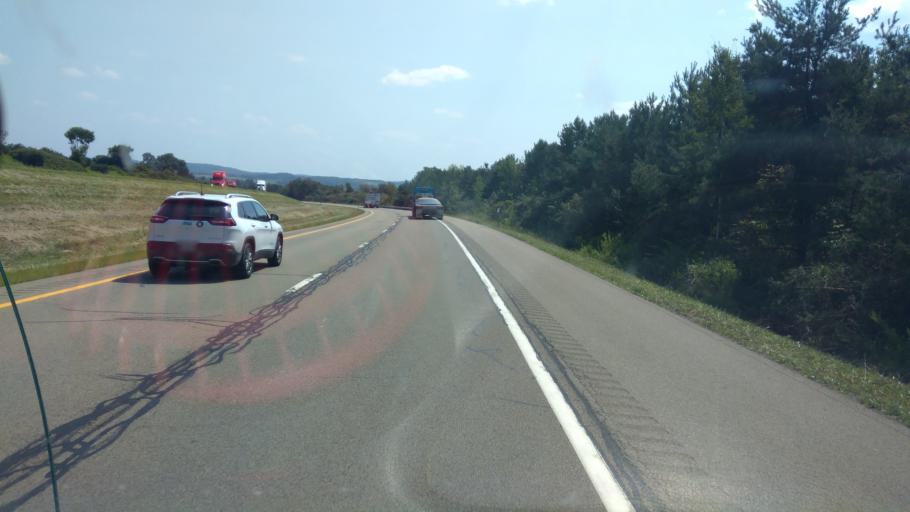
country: US
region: New York
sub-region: Steuben County
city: Canisteo
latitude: 42.3715
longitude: -77.5231
